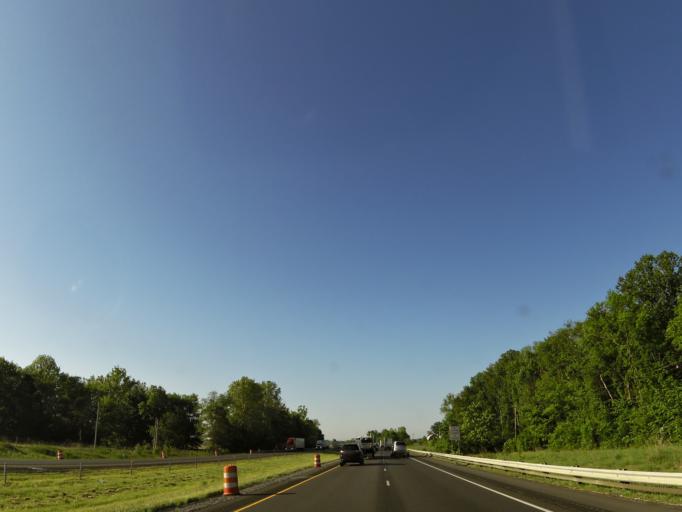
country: US
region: Indiana
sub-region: Jackson County
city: Seymour
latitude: 38.9439
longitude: -85.8434
